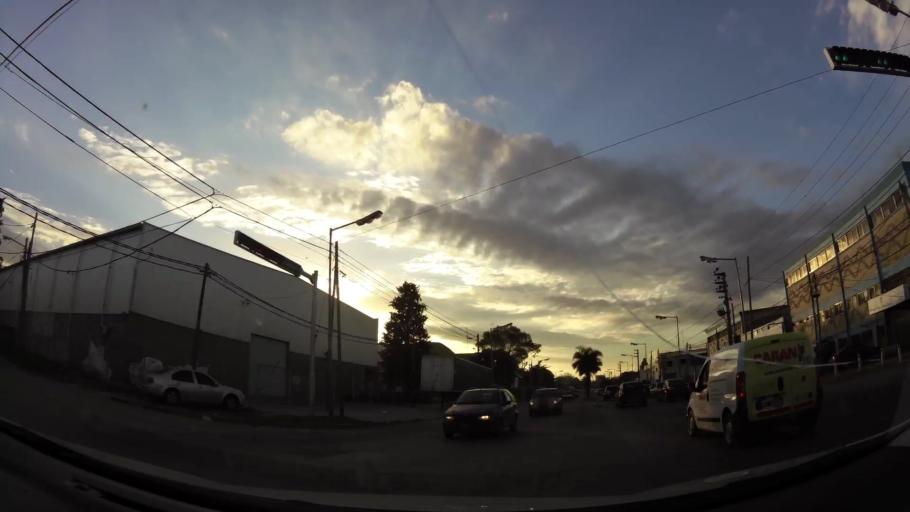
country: AR
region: Buenos Aires
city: Santa Catalina - Dique Lujan
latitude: -34.4498
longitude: -58.6626
